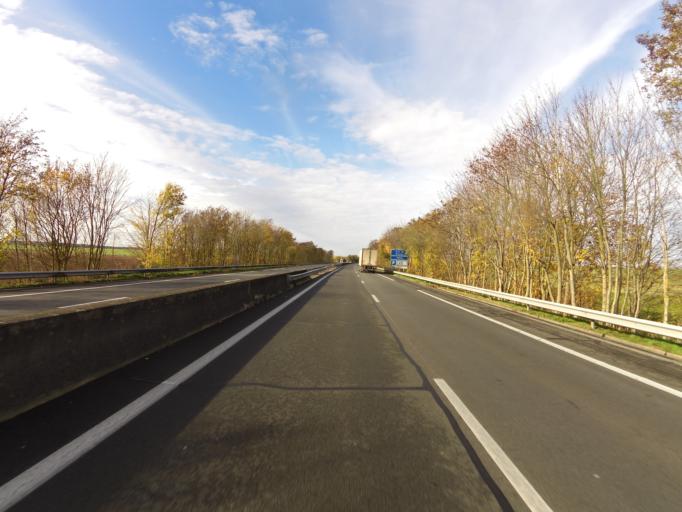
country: FR
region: Picardie
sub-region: Departement de l'Aisne
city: Couvron-et-Aumencourt
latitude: 49.6609
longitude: 3.5439
